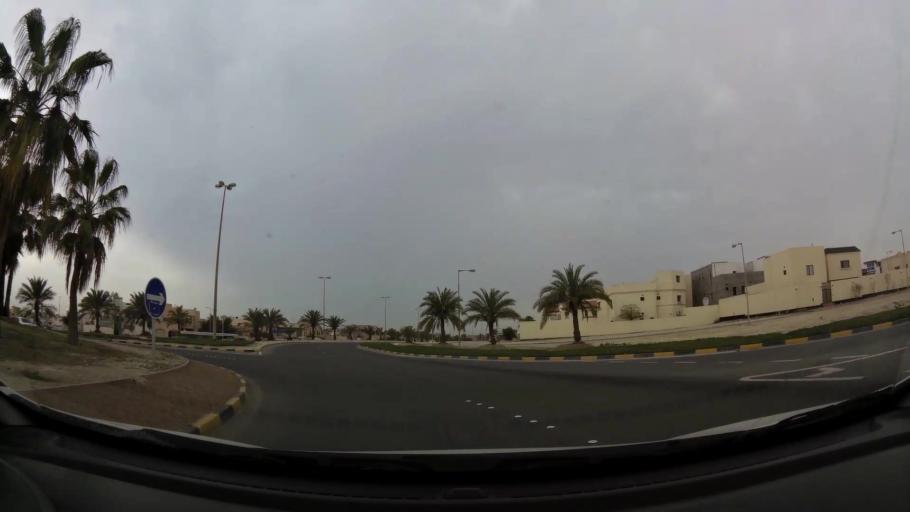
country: BH
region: Central Governorate
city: Madinat Hamad
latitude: 26.0920
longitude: 50.5097
